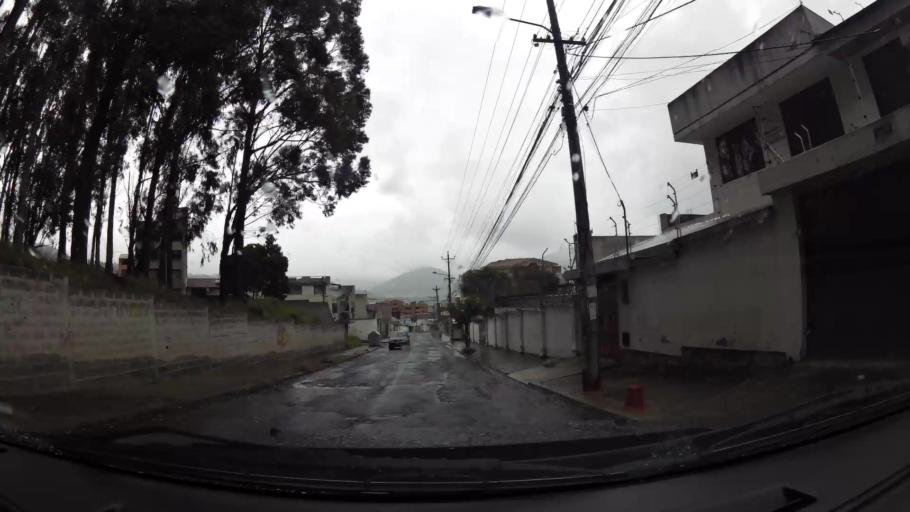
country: EC
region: Pichincha
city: Quito
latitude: -0.1098
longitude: -78.5012
